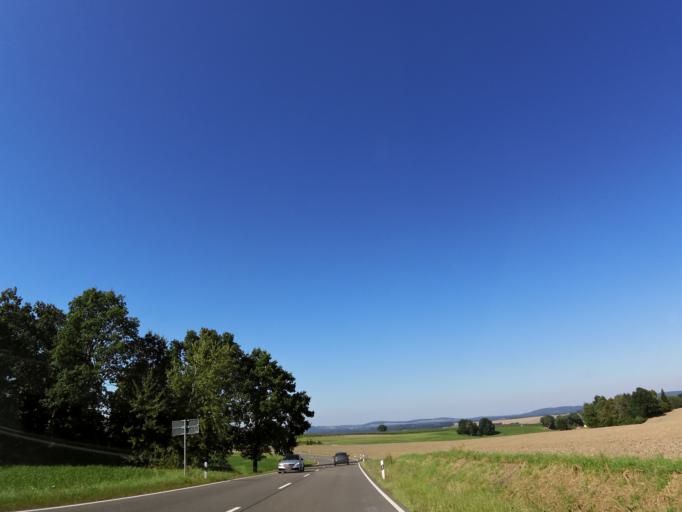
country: DE
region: Saxony
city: Struppen
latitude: 50.9257
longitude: 13.9850
